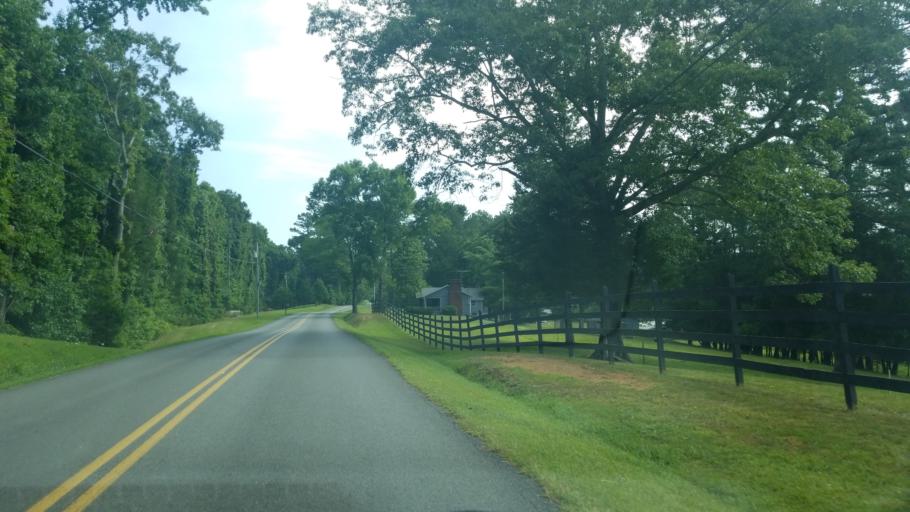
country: US
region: Tennessee
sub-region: Hamilton County
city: Apison
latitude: 35.0463
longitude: -84.9897
